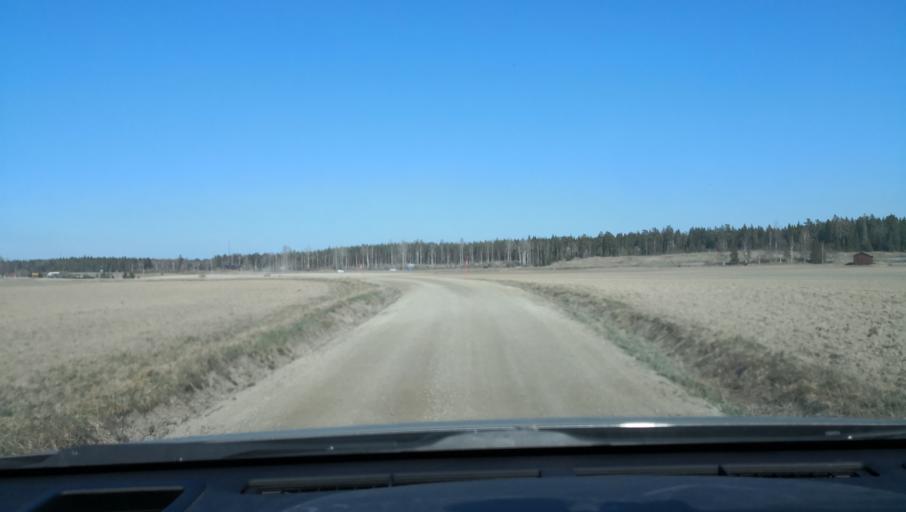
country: SE
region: Vaestmanland
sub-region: Sala Kommun
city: Sala
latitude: 59.9006
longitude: 16.5288
